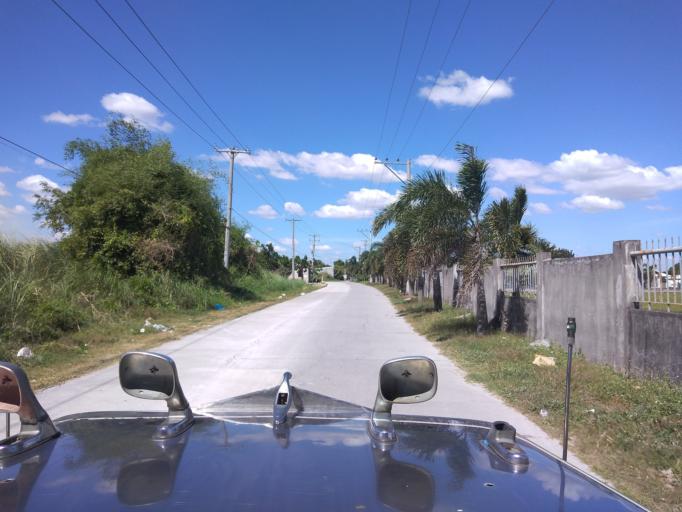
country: PH
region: Central Luzon
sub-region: Province of Pampanga
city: Magliman
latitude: 15.0273
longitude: 120.6514
